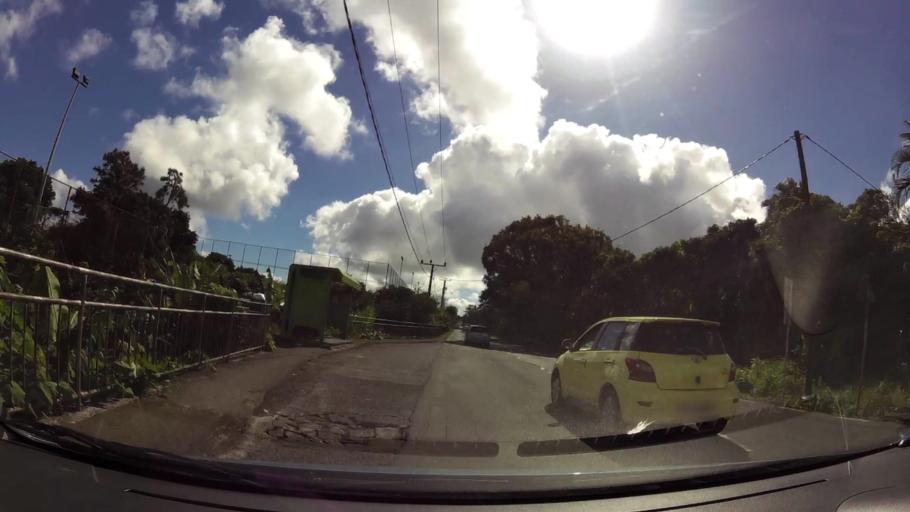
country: MU
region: Plaines Wilhems
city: Midlands
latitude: -20.3416
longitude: 57.5446
